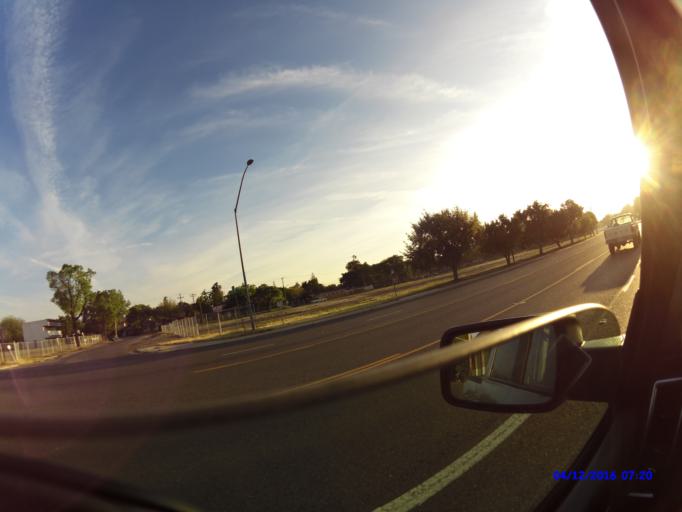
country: US
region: California
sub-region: Stanislaus County
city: Modesto
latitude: 37.6373
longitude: -120.9871
